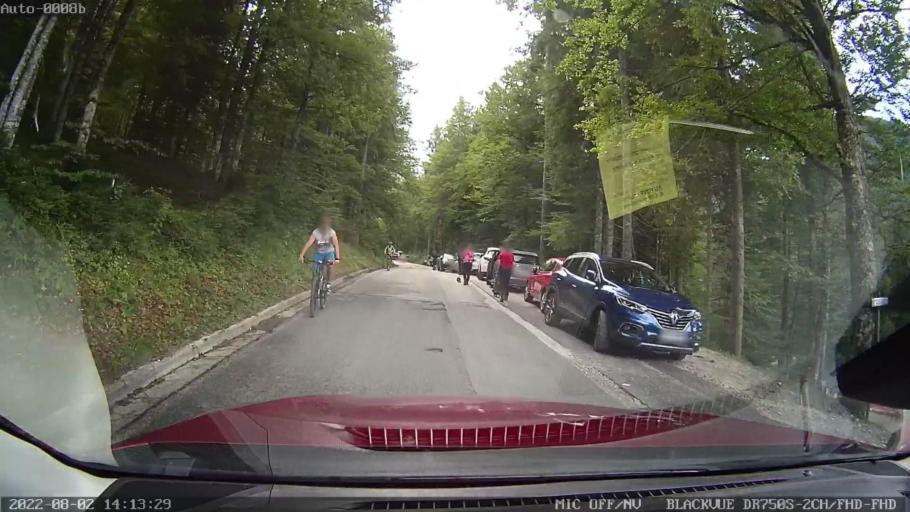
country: AT
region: Carinthia
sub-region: Politischer Bezirk Villach Land
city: Arnoldstein
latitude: 46.4804
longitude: 13.6732
